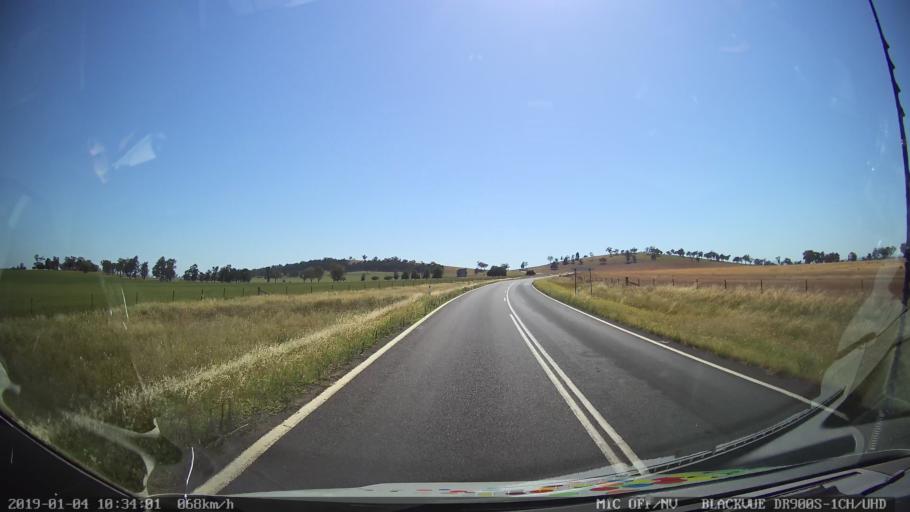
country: AU
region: New South Wales
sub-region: Cabonne
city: Canowindra
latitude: -33.3169
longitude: 148.6561
